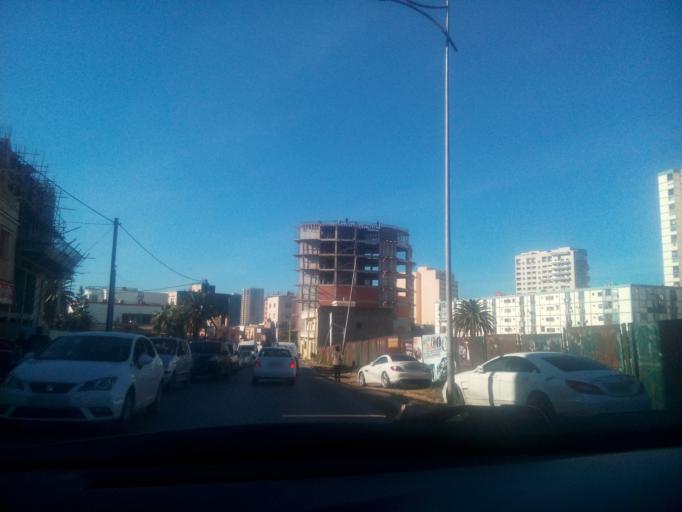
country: DZ
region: Oran
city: Oran
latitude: 35.7135
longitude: -0.6141
